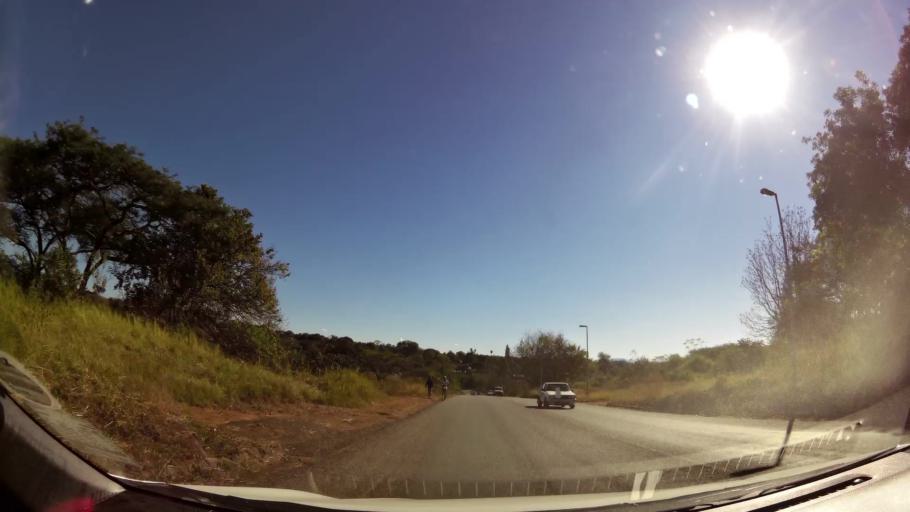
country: ZA
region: Limpopo
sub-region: Mopani District Municipality
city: Tzaneen
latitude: -23.8418
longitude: 30.1670
